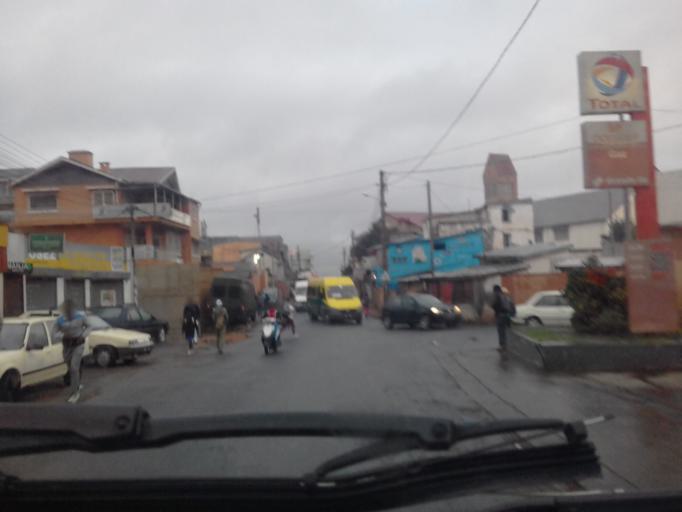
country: MG
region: Analamanga
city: Antananarivo
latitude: -18.8738
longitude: 47.5503
